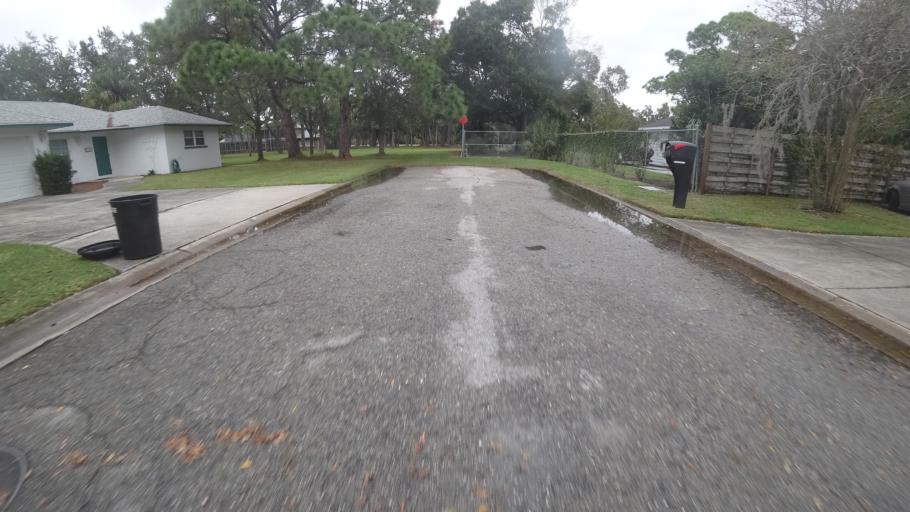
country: US
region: Florida
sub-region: Manatee County
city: West Bradenton
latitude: 27.5175
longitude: -82.6436
